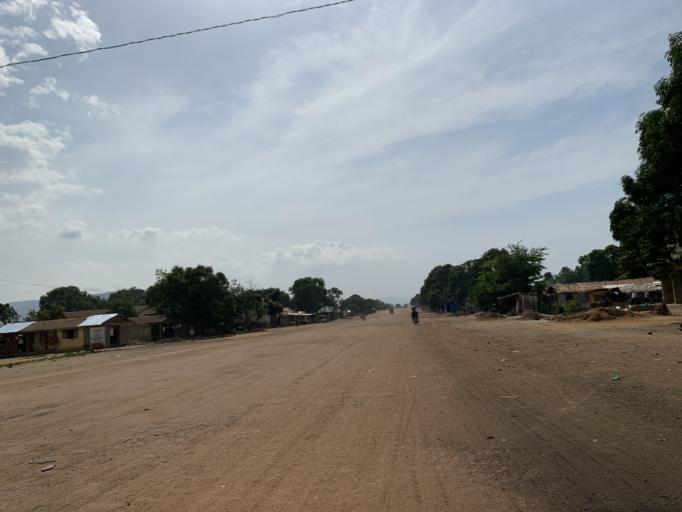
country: SL
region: Western Area
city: Waterloo
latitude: 8.3376
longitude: -13.0439
